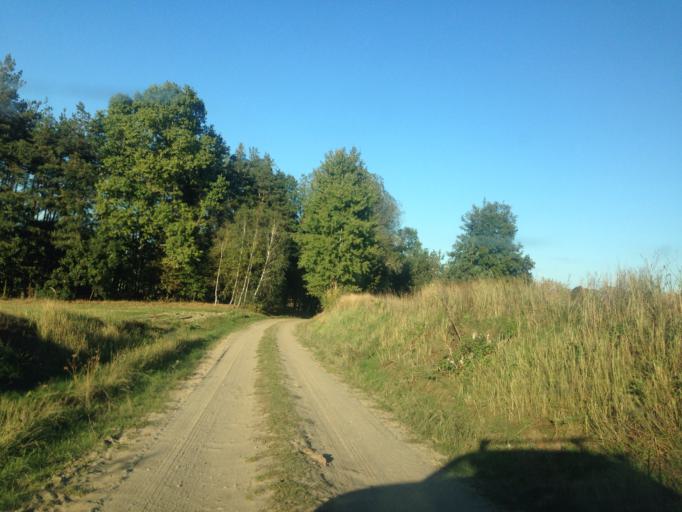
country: PL
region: Kujawsko-Pomorskie
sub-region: Powiat brodnicki
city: Bartniczka
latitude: 53.2790
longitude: 19.6837
